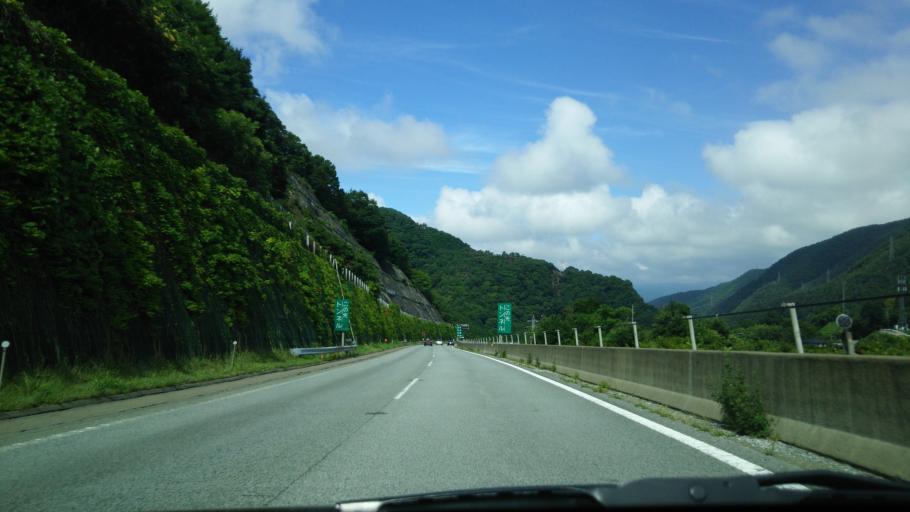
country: JP
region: Yamanashi
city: Enzan
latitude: 35.6404
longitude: 138.7718
